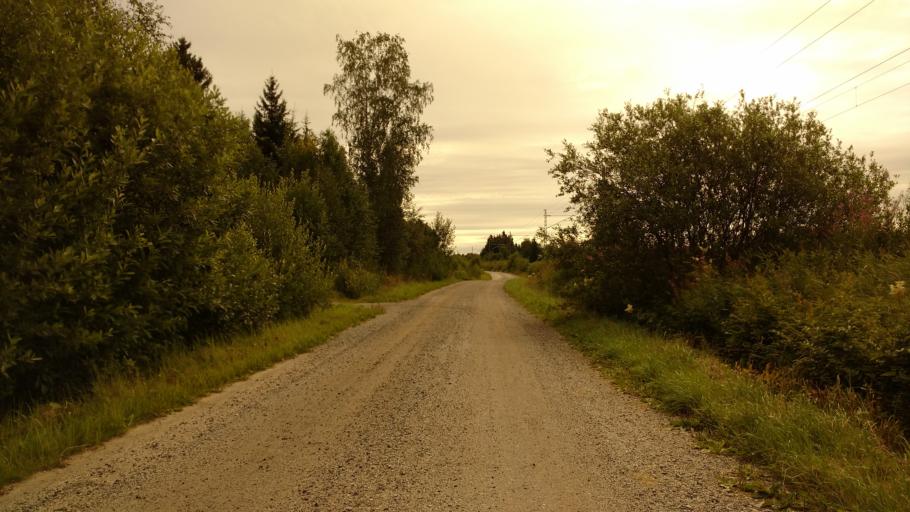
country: FI
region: Varsinais-Suomi
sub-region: Turku
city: Kaarina
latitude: 60.4440
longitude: 22.4227
